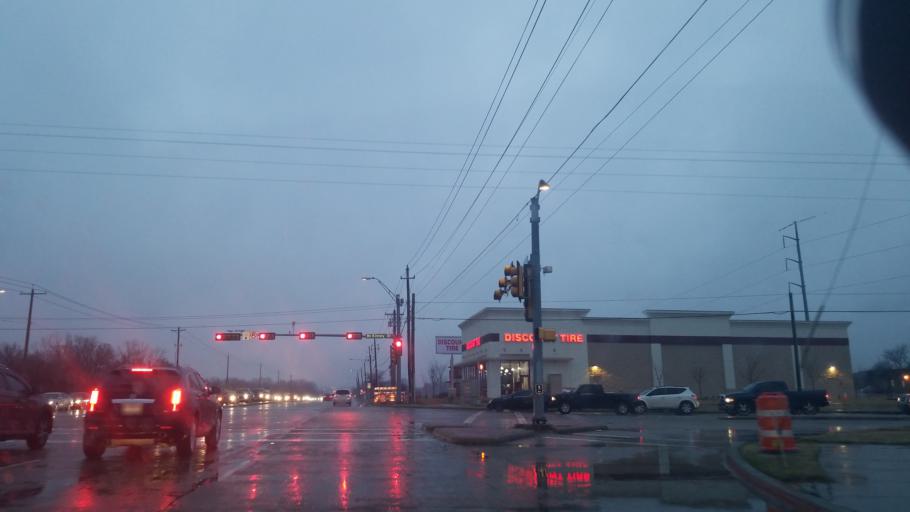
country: US
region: Texas
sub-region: Denton County
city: Denton
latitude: 33.2134
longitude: -97.0908
